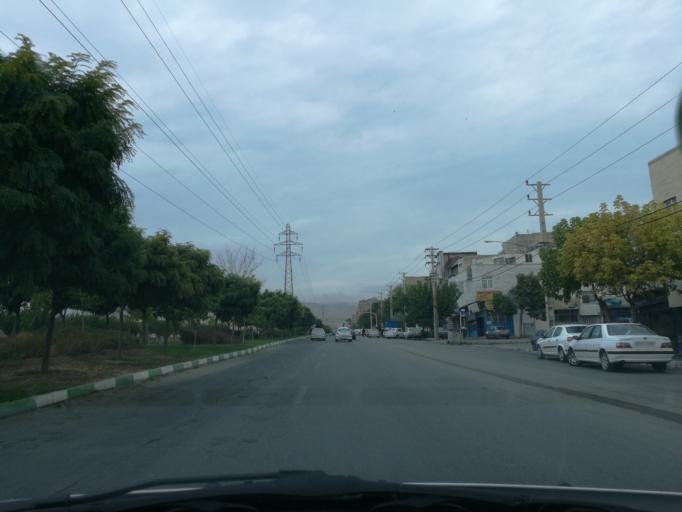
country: IR
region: Alborz
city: Karaj
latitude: 35.8508
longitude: 50.9179
